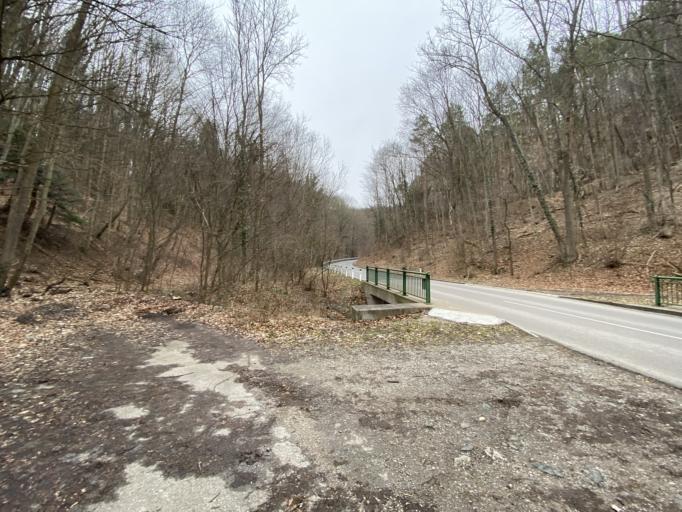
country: AT
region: Lower Austria
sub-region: Politischer Bezirk Modling
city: Gaaden
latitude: 48.0207
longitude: 16.1904
